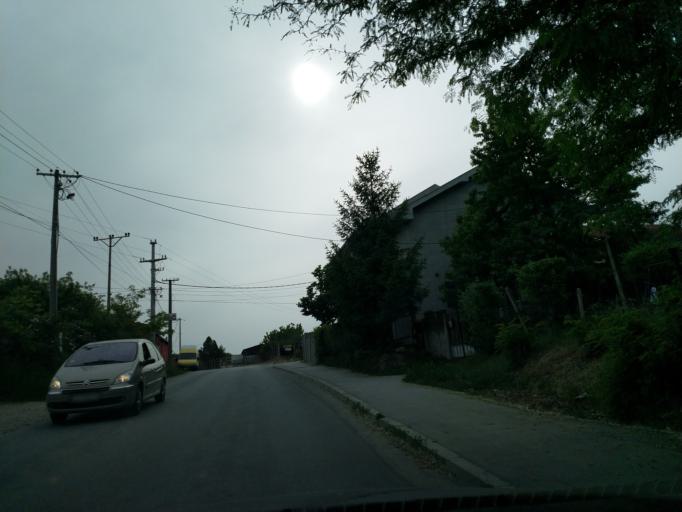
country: RS
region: Central Serbia
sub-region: Pomoravski Okrug
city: Jagodina
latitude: 43.9762
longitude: 21.2439
